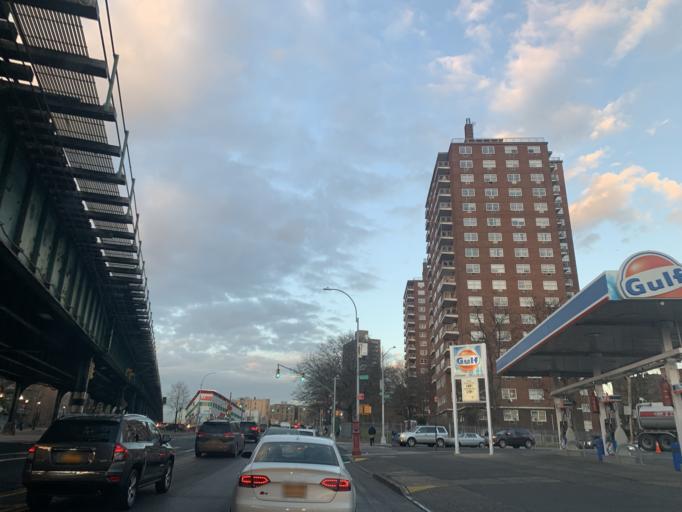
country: US
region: New York
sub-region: Bronx
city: The Bronx
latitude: 40.8592
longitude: -73.8674
